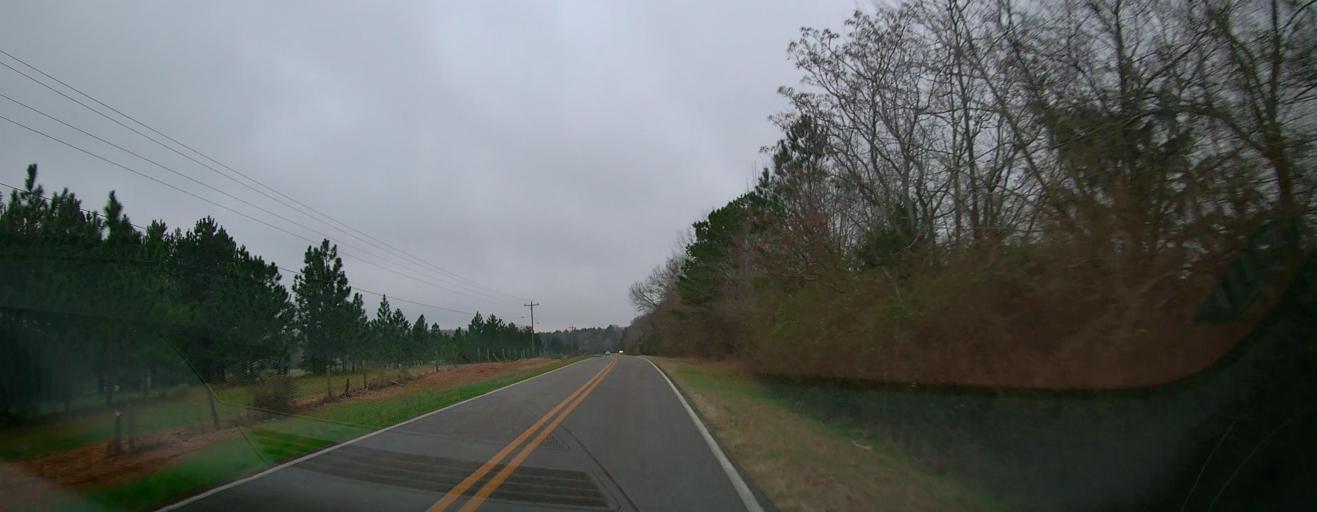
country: US
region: Georgia
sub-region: Lamar County
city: Barnesville
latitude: 33.1004
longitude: -84.0557
